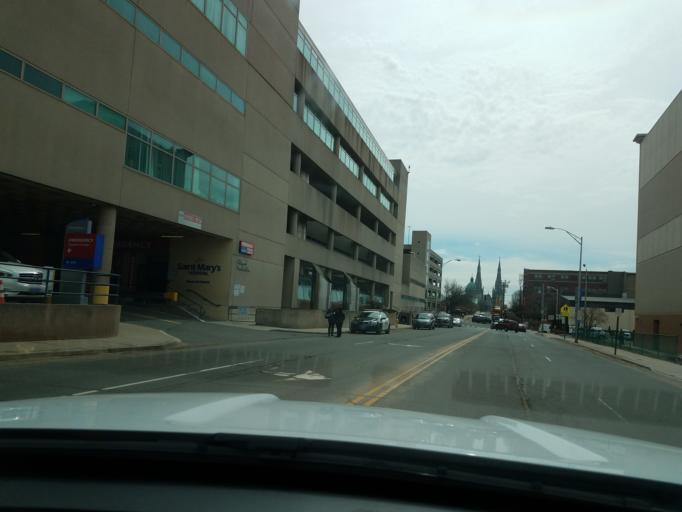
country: US
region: Connecticut
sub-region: New Haven County
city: Waterbury
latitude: 41.5534
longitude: -73.0374
